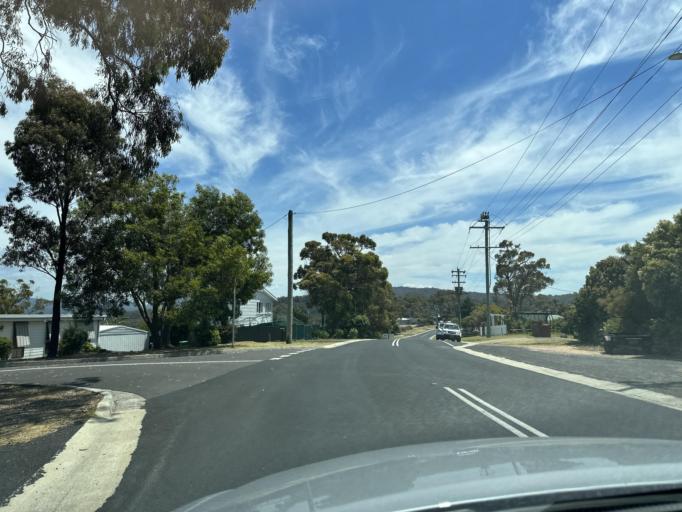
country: AU
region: New South Wales
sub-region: Bega Valley
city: Merimbula
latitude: -36.8906
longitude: 149.8983
